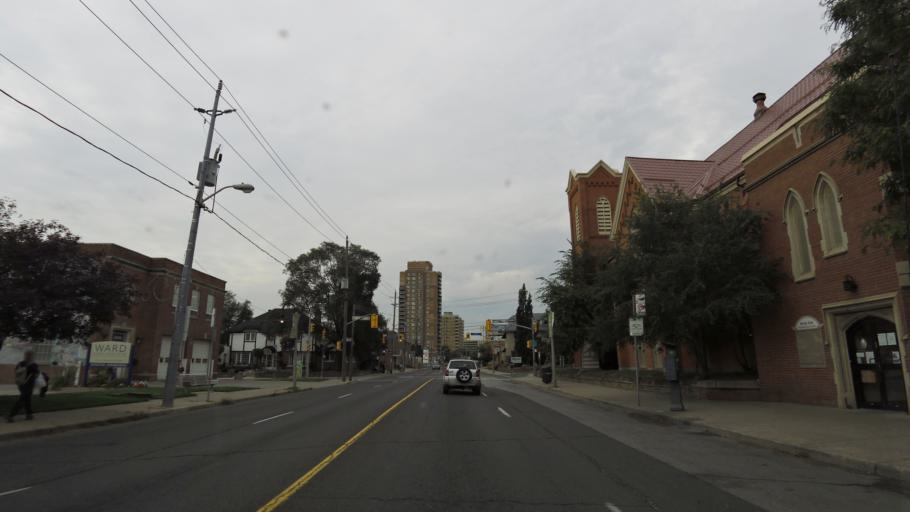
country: CA
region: Ontario
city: Etobicoke
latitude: 43.7011
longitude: -79.5199
